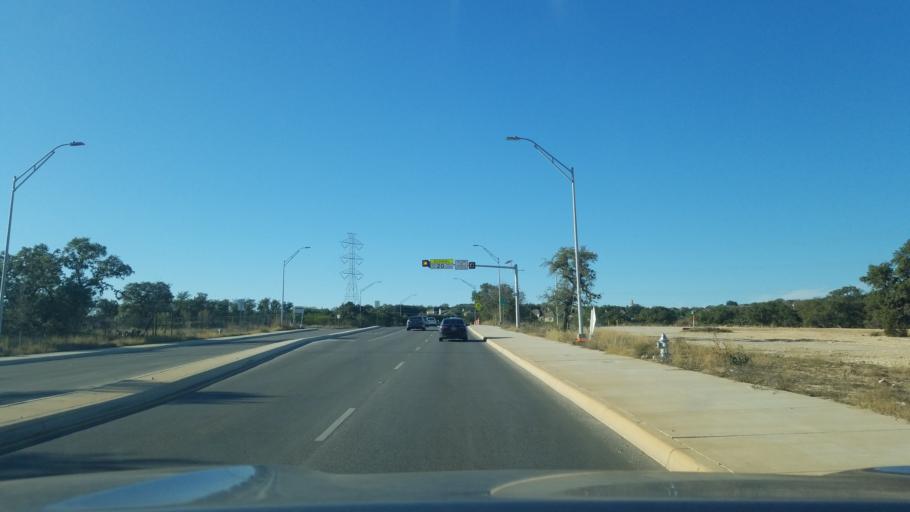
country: US
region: Texas
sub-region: Bexar County
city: Hollywood Park
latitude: 29.6297
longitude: -98.4793
